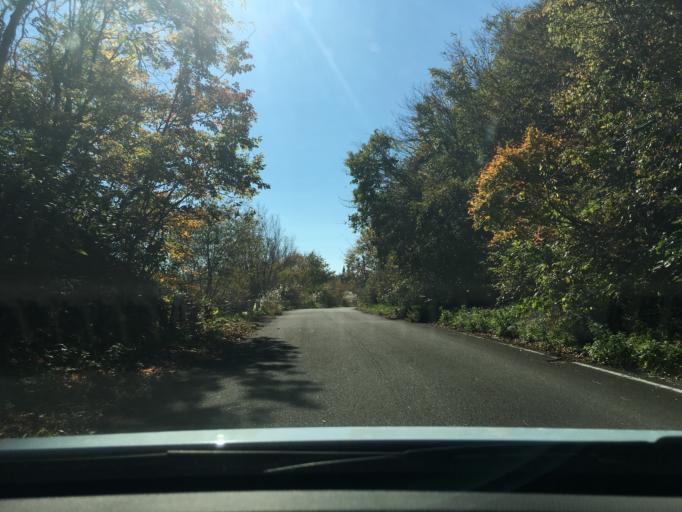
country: JP
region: Fukushima
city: Inawashiro
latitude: 37.4028
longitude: 140.0241
